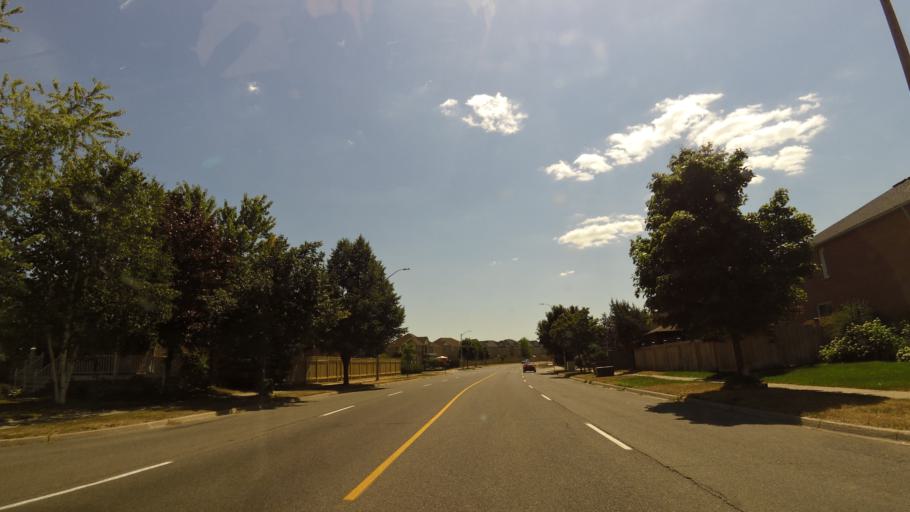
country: CA
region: Ontario
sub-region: Halton
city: Milton
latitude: 43.6350
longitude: -79.8767
